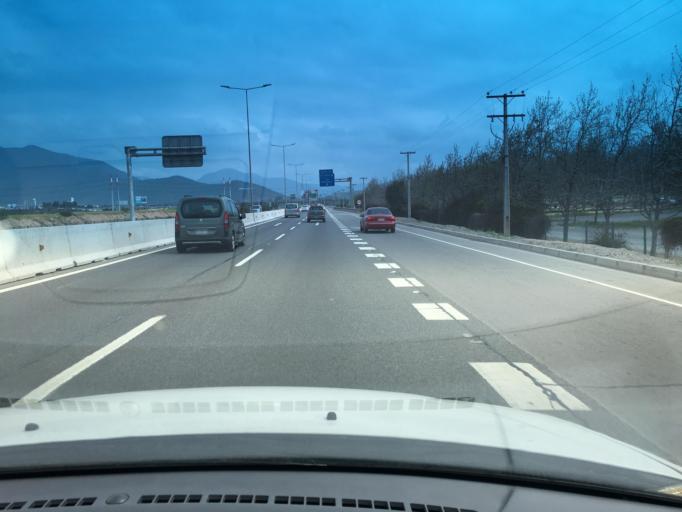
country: CL
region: Santiago Metropolitan
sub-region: Provincia de Santiago
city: Lo Prado
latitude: -33.4269
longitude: -70.8028
